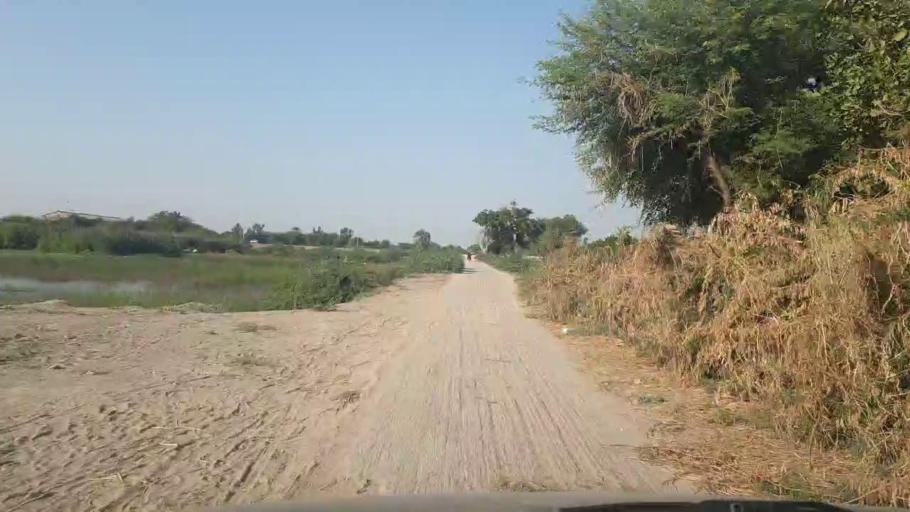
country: PK
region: Sindh
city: Badin
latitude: 24.6525
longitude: 68.8152
